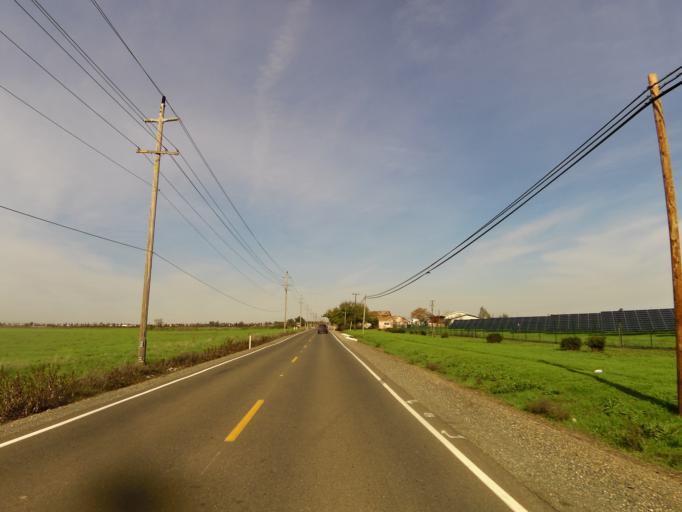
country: US
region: California
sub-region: Sacramento County
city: Laguna
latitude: 38.3661
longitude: -121.4176
